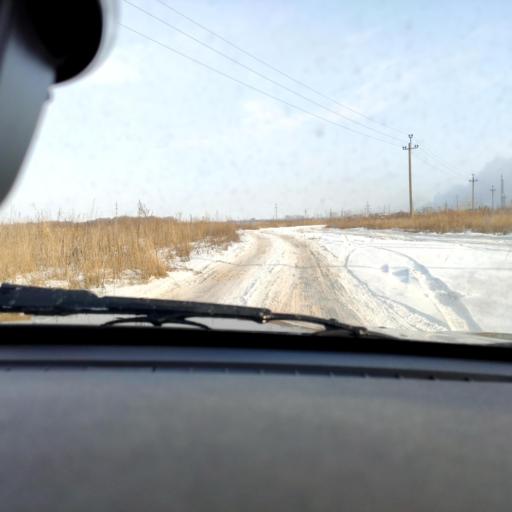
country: RU
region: Samara
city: Tol'yatti
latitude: 53.5437
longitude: 49.4191
